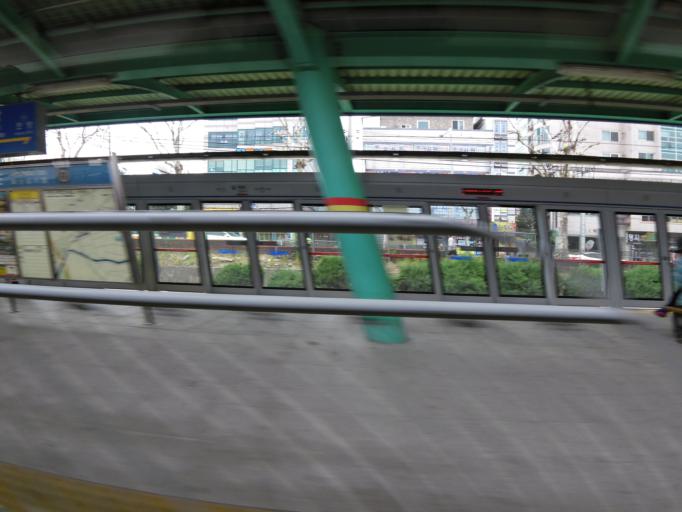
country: KR
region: Gyeonggi-do
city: Anyang-si
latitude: 37.3846
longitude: 126.9354
